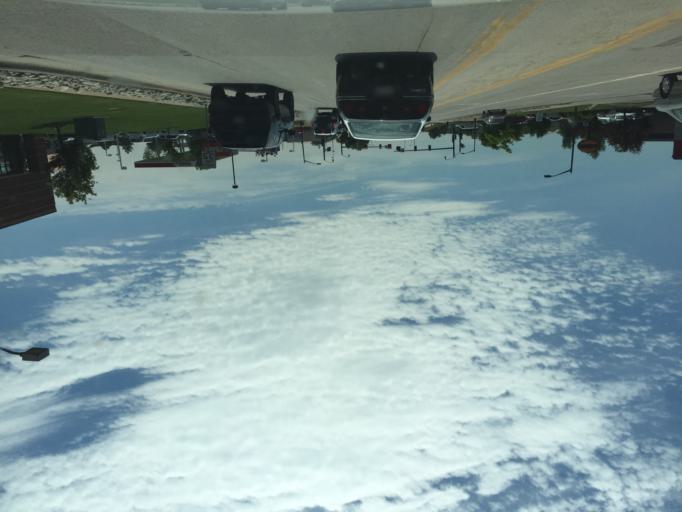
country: US
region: Colorado
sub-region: Douglas County
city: Castle Rock
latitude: 39.3657
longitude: -104.8627
